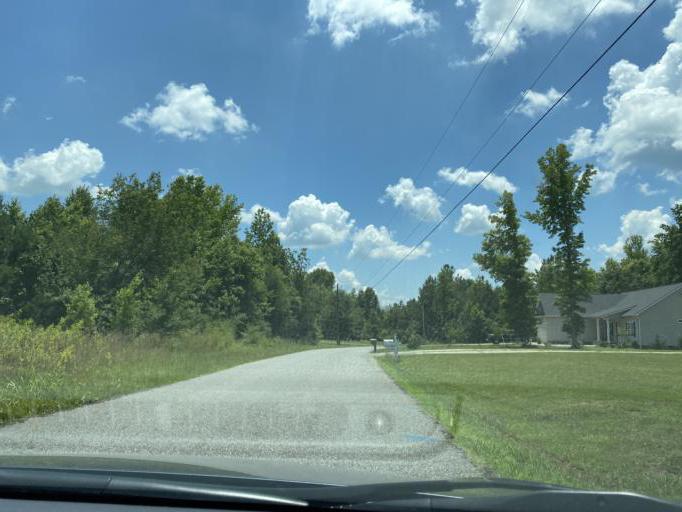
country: US
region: South Carolina
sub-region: Cherokee County
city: Gaffney
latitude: 35.1295
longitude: -81.7189
